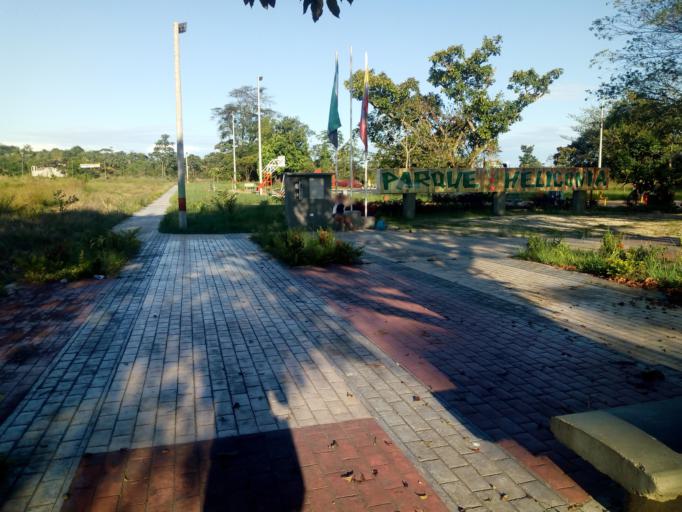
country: CO
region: Putumayo
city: Villagarzon
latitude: 1.0088
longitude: -76.6138
